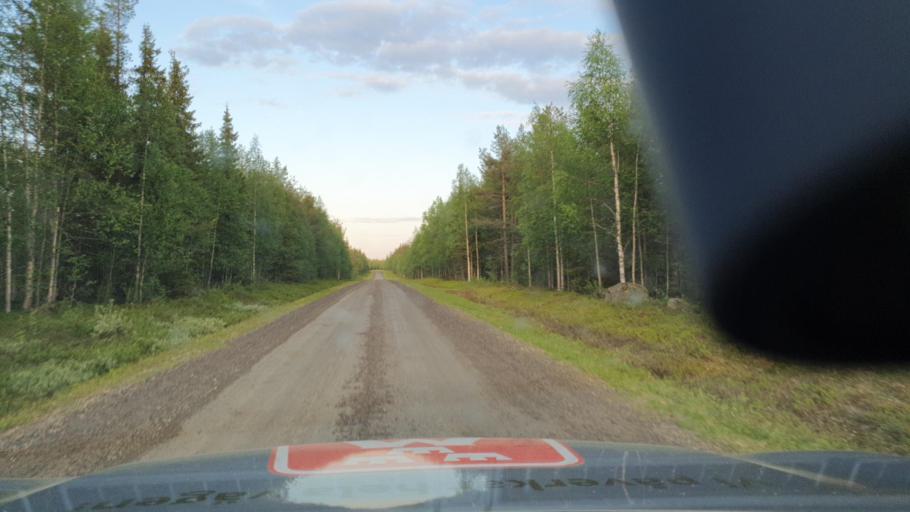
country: SE
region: Norrbotten
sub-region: Bodens Kommun
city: Boden
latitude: 66.4912
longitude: 21.5775
